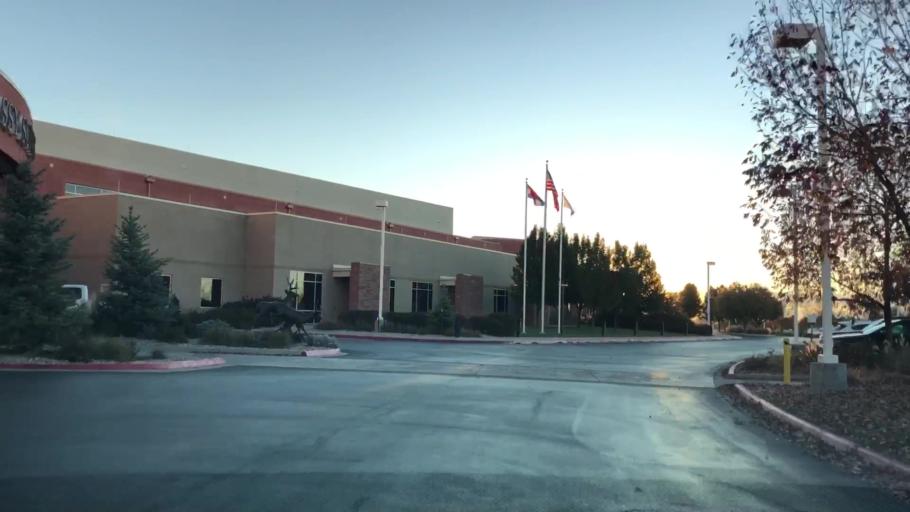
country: US
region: Colorado
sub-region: Larimer County
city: Loveland
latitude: 40.4403
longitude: -104.9908
